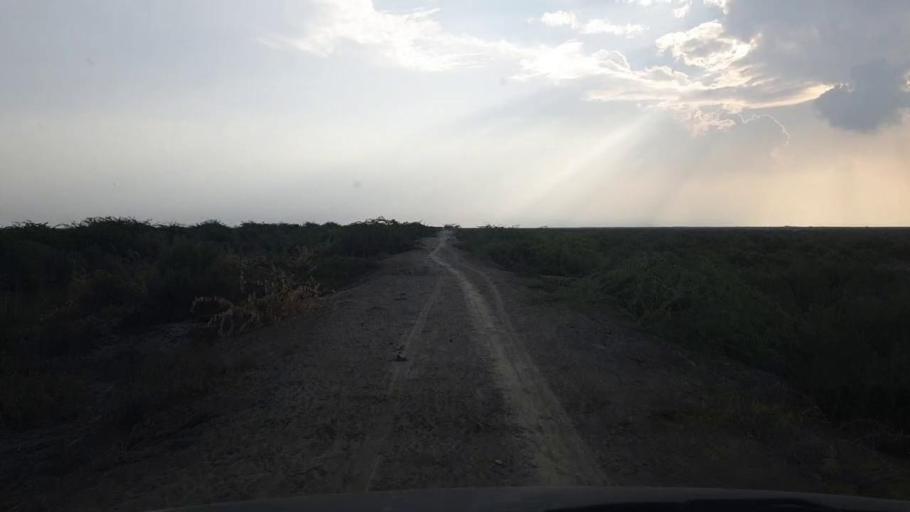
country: PK
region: Sindh
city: Badin
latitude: 24.4566
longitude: 68.6869
